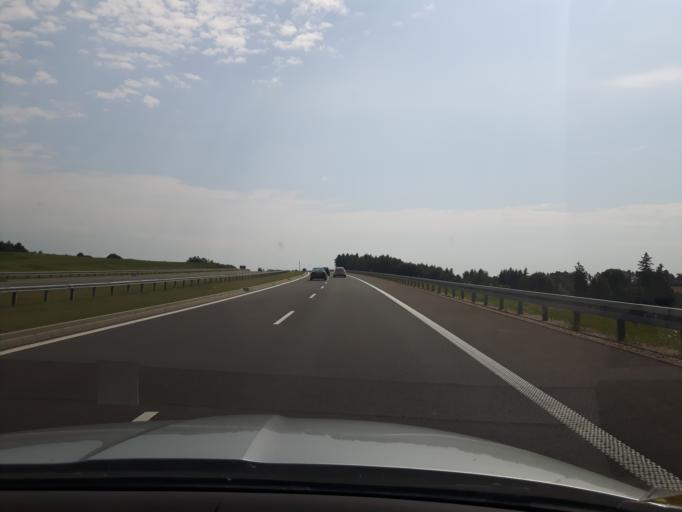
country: PL
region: Warmian-Masurian Voivodeship
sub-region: Powiat nidzicki
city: Nidzica
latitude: 53.3505
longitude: 20.3920
